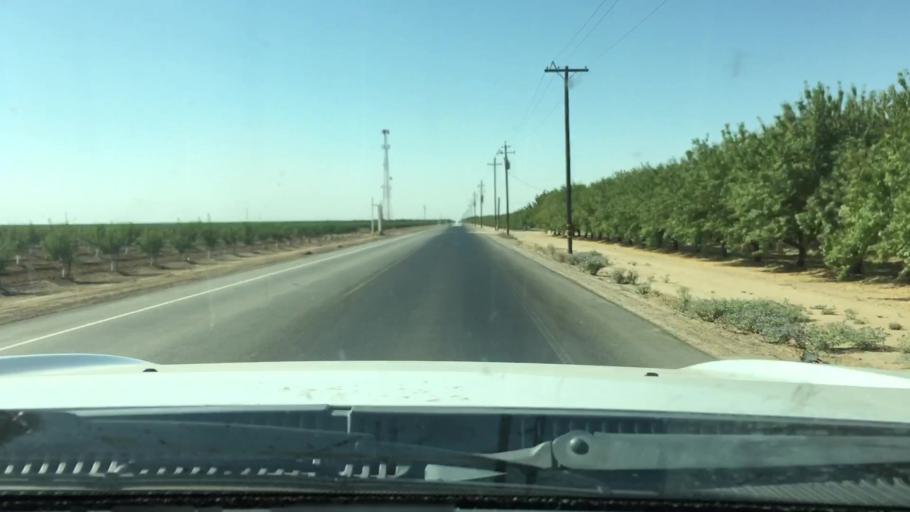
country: US
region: California
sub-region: Kern County
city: Wasco
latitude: 35.5915
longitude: -119.4737
